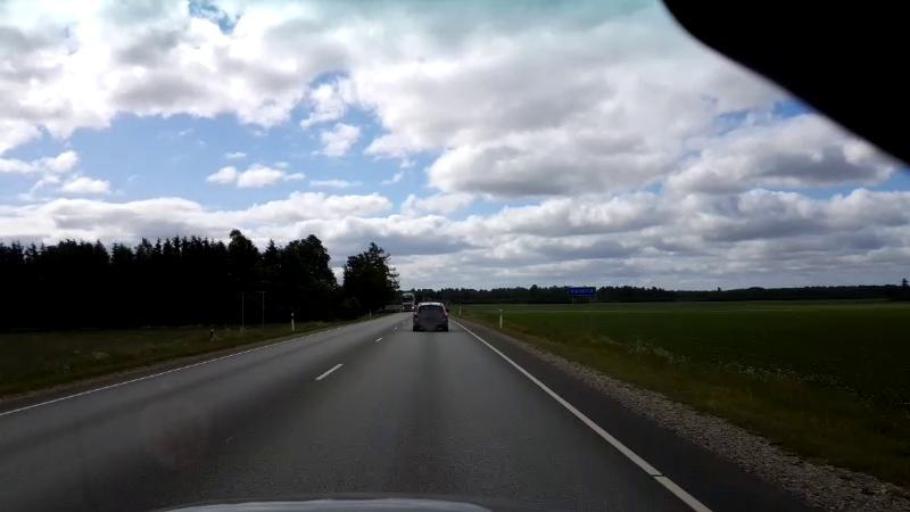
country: EE
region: Paernumaa
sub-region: Halinga vald
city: Parnu-Jaagupi
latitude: 58.5678
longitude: 24.5139
